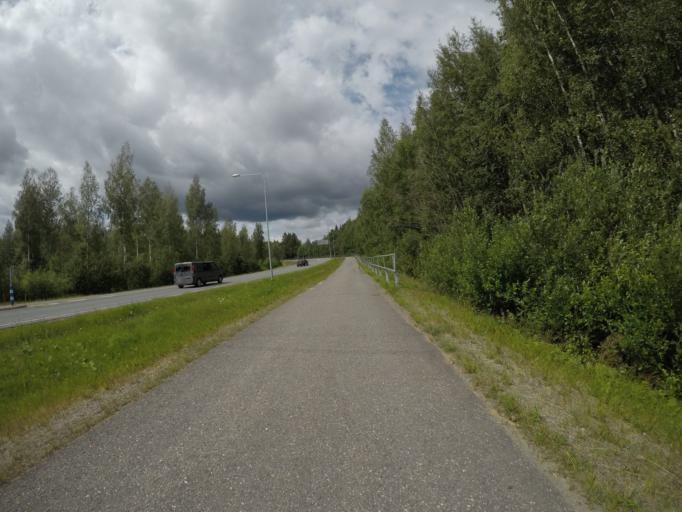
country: FI
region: Haeme
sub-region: Haemeenlinna
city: Haemeenlinna
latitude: 60.9653
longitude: 24.4507
